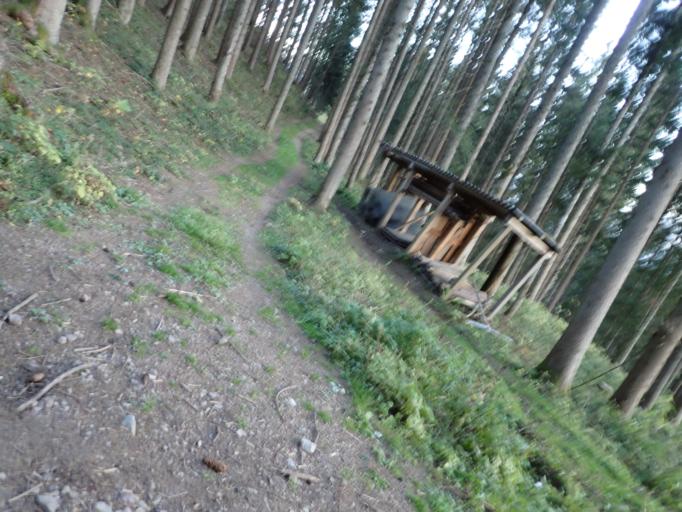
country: AT
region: Salzburg
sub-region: Politischer Bezirk Sankt Johann im Pongau
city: Pfarrwerfen
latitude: 47.4776
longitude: 13.2165
